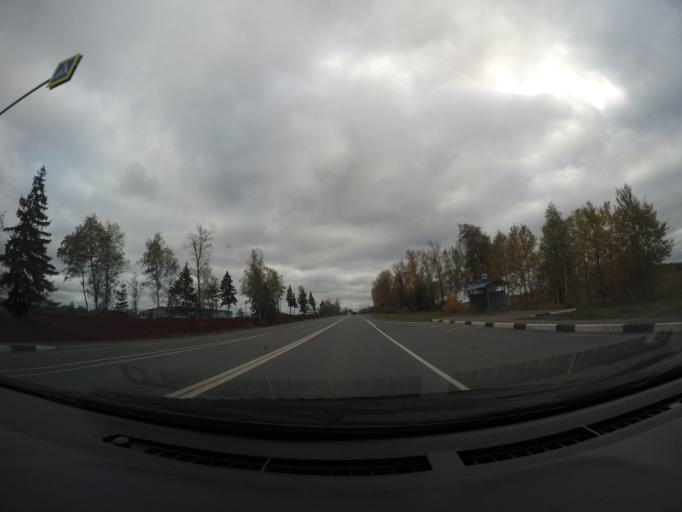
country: RU
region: Moskovskaya
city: Dorokhovo
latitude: 55.5977
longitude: 36.3608
